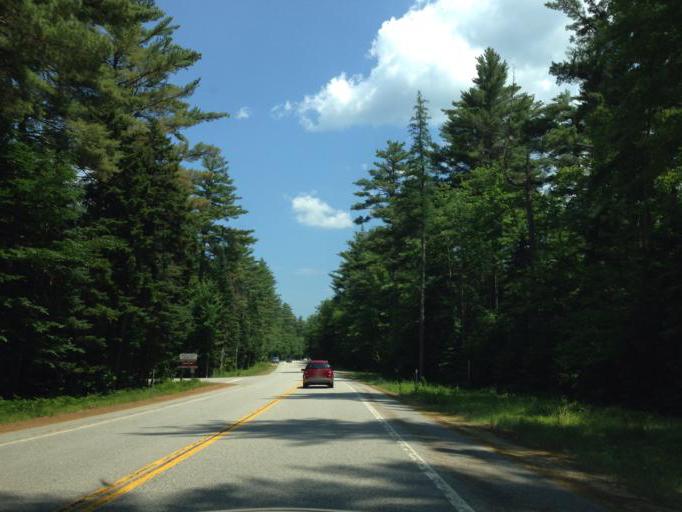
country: US
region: New Hampshire
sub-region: Carroll County
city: Tamworth
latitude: 43.9951
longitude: -71.3382
